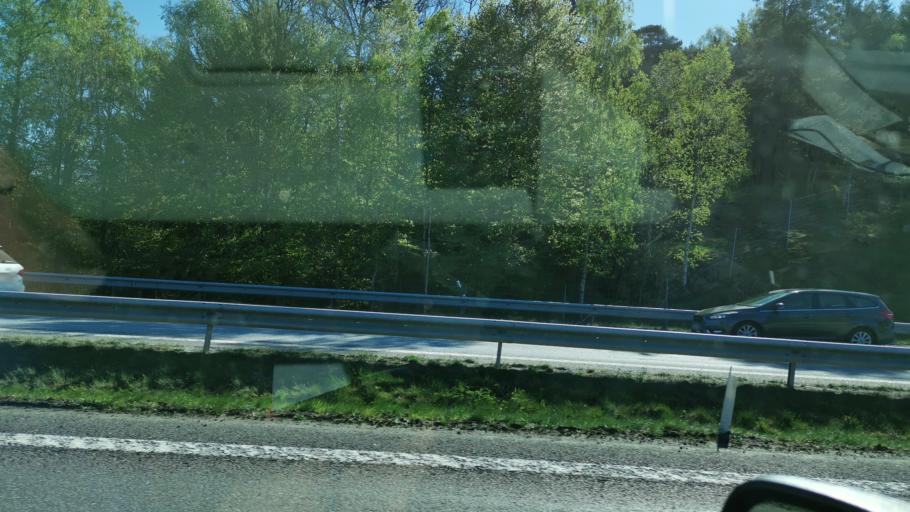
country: SE
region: Vaestra Goetaland
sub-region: Uddevalla Kommun
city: Ljungskile
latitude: 58.1985
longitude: 11.9076
